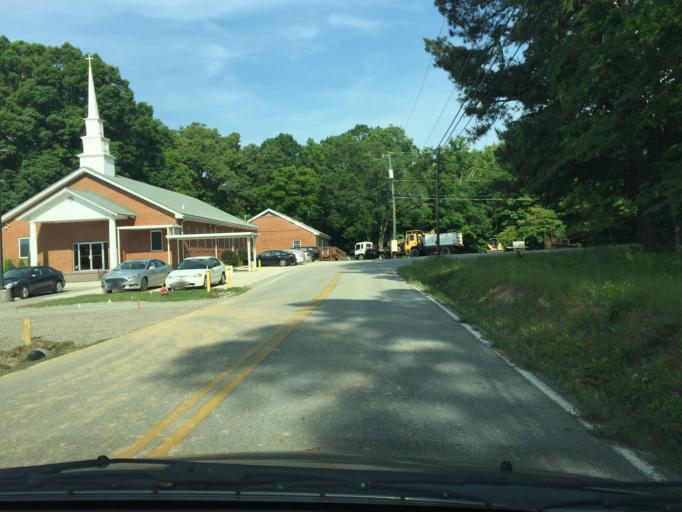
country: US
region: Tennessee
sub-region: Hamilton County
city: Collegedale
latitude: 35.0898
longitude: -85.0154
